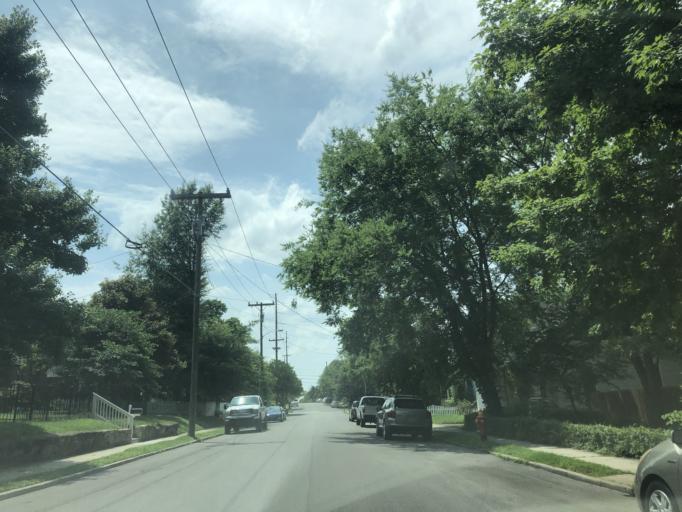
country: US
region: Tennessee
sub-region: Davidson County
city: Nashville
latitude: 36.1777
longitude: -86.7404
